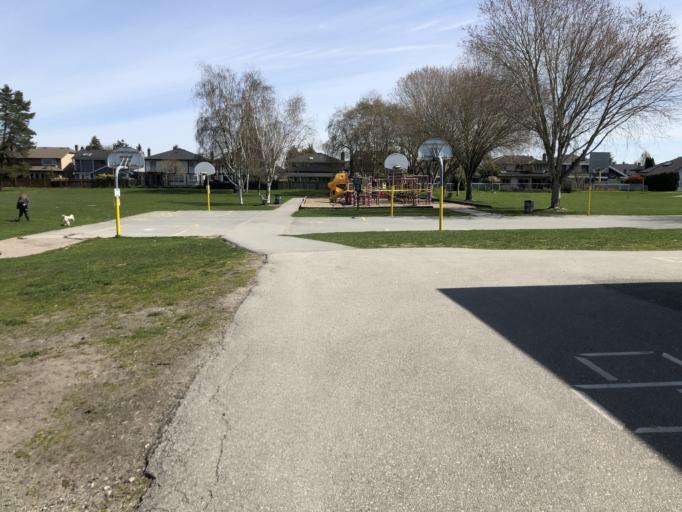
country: CA
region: British Columbia
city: Richmond
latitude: 49.1509
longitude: -123.1183
